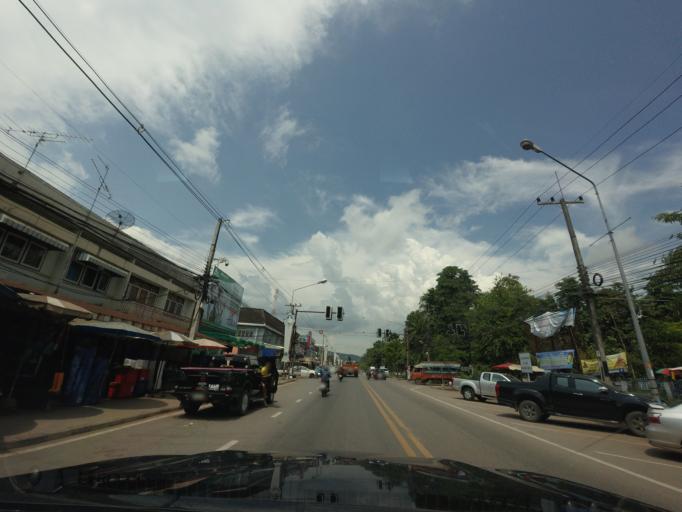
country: TH
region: Khon Kaen
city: Phu Wiang
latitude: 16.6539
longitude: 102.3760
